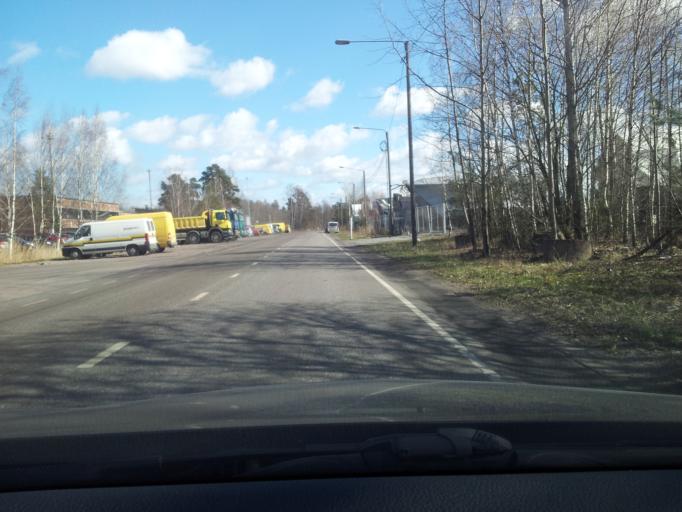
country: FI
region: Uusimaa
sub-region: Helsinki
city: Koukkuniemi
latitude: 60.1481
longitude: 24.7172
